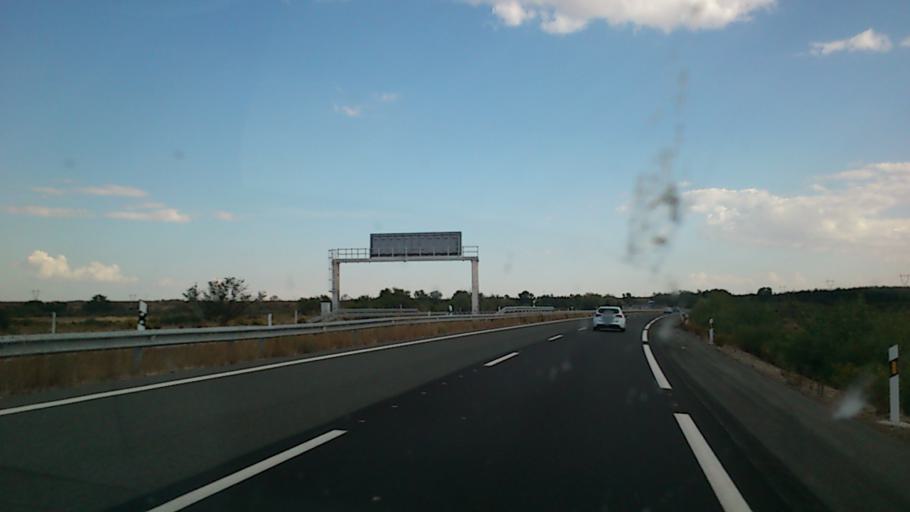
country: ES
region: Navarre
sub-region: Provincia de Navarra
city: Corella
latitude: 42.1290
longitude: -1.7592
